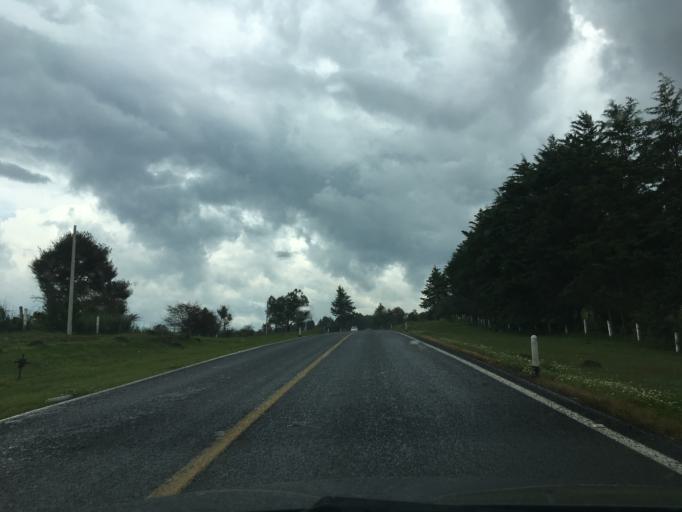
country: MX
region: Michoacan
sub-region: Patzcuaro
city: Santa Ana Chapitiro
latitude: 19.5113
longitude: -101.6757
